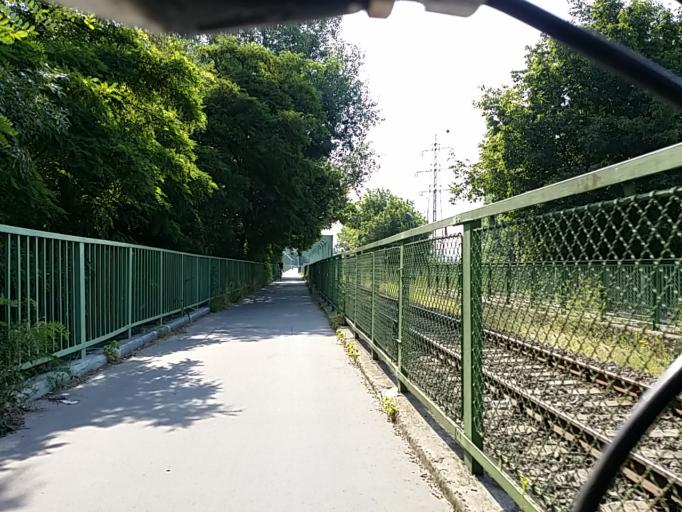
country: HU
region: Budapest
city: Budapest IV. keruelet
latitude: 47.5614
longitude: 19.0736
